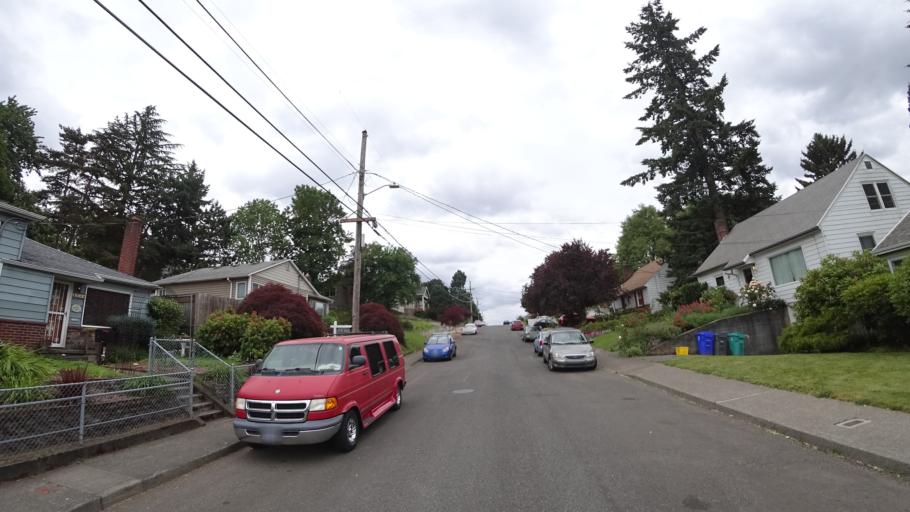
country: US
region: Oregon
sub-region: Multnomah County
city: Lents
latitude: 45.4895
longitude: -122.5759
